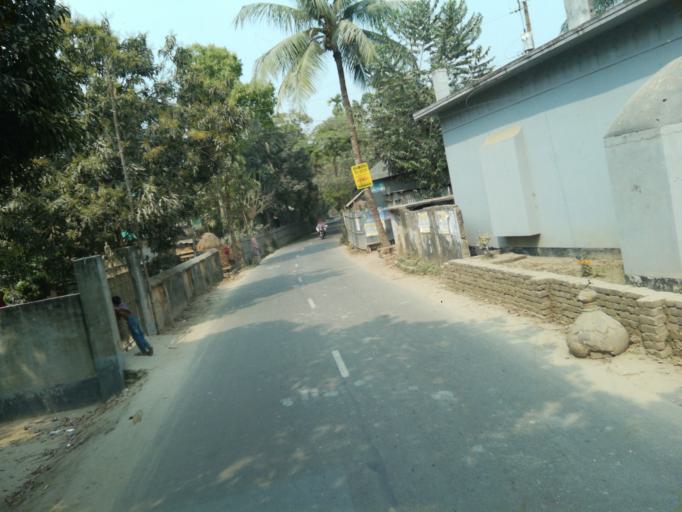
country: BD
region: Dhaka
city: Nagarpur
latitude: 23.9811
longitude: 89.8438
